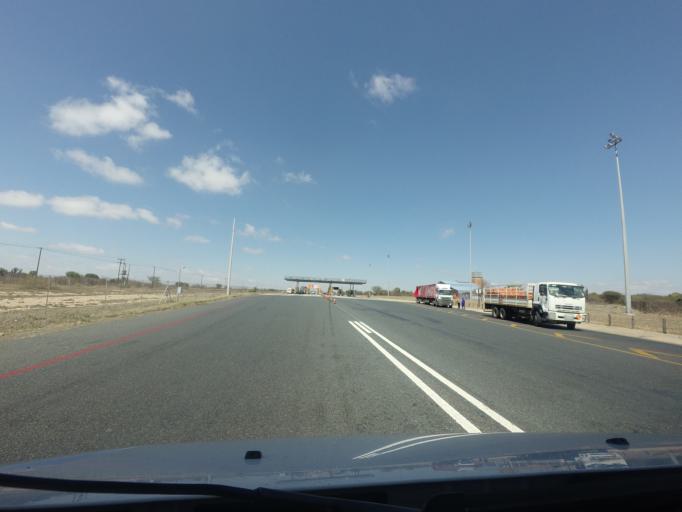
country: ZA
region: Limpopo
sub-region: Vhembe District Municipality
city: Louis Trichardt
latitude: -23.3660
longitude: 29.7758
